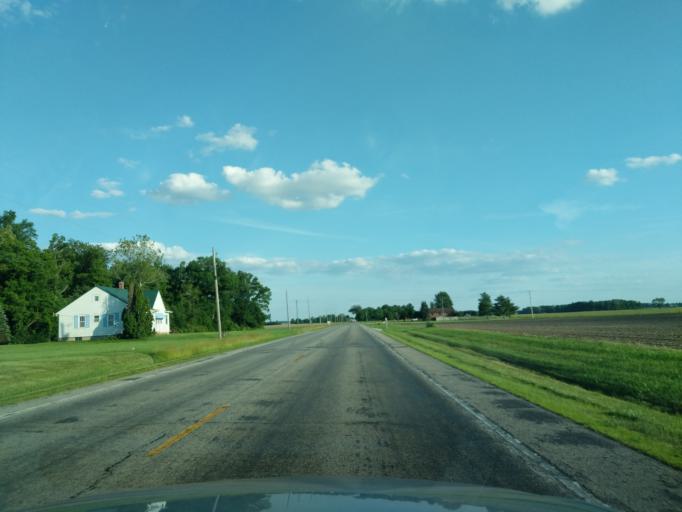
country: US
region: Indiana
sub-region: Huntington County
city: Huntington
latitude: 40.8018
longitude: -85.4611
